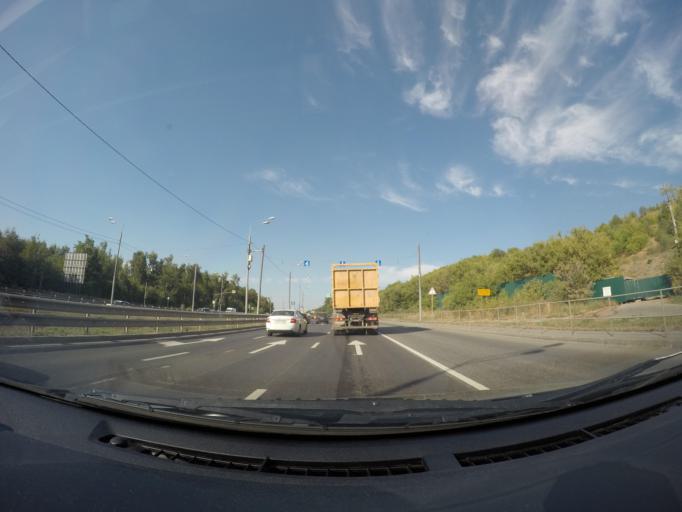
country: RU
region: Moscow
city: Businovo
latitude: 55.9037
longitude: 37.4923
